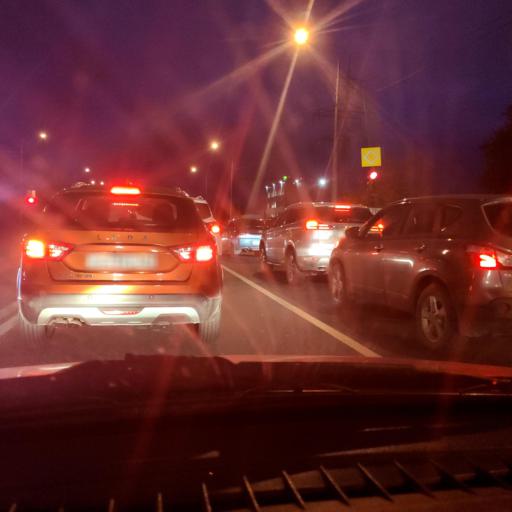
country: RU
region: Samara
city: Tol'yatti
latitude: 53.5694
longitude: 49.2917
